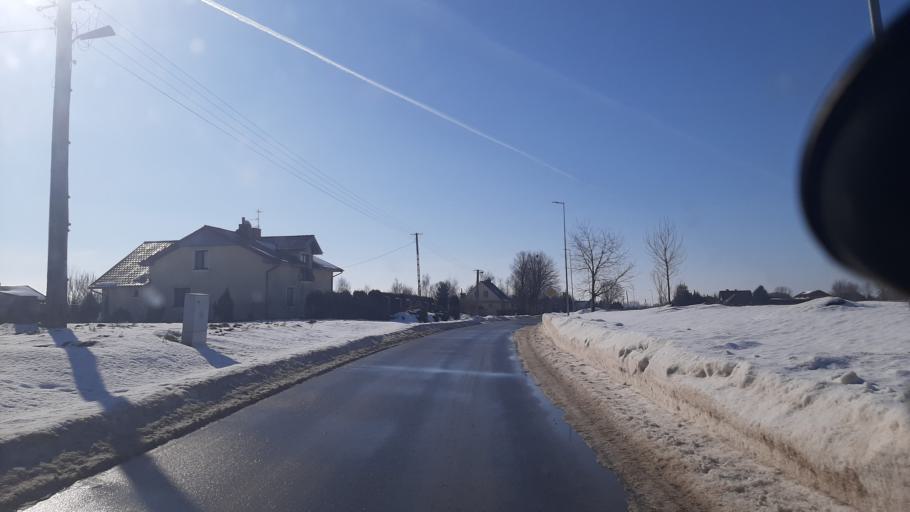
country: PL
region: Lublin Voivodeship
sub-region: Powiat lubelski
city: Garbow
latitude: 51.2972
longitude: 22.3045
